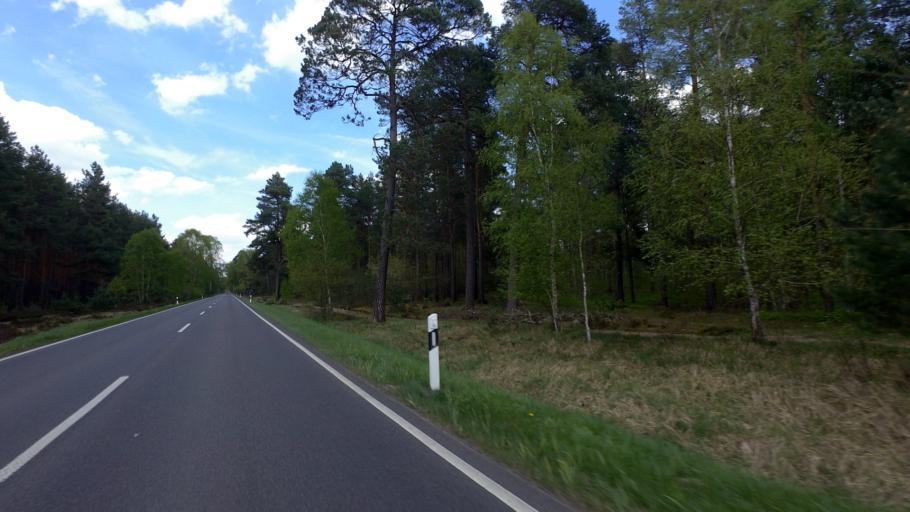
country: DE
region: Brandenburg
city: Marienwerder
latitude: 52.9713
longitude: 13.5766
